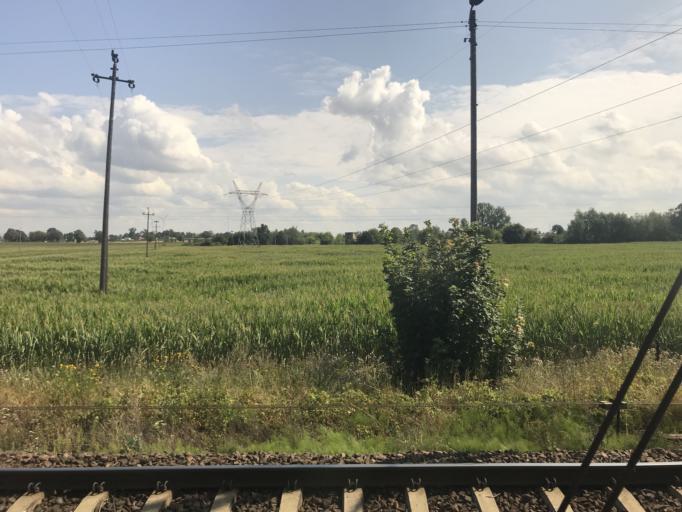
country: PL
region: Kujawsko-Pomorskie
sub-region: Powiat inowroclawski
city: Zlotniki Kujawskie
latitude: 52.9117
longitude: 18.1386
